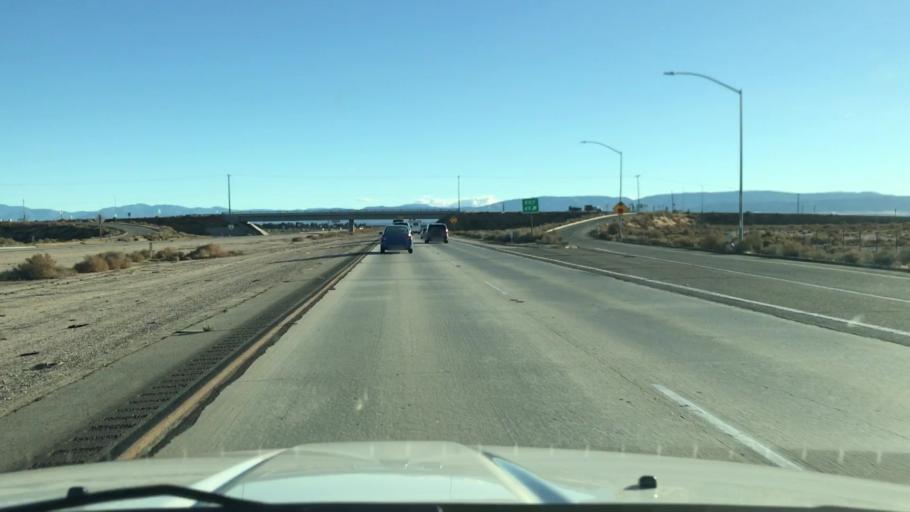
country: US
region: California
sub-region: Kern County
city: Rosamond
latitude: 34.7797
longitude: -118.1709
